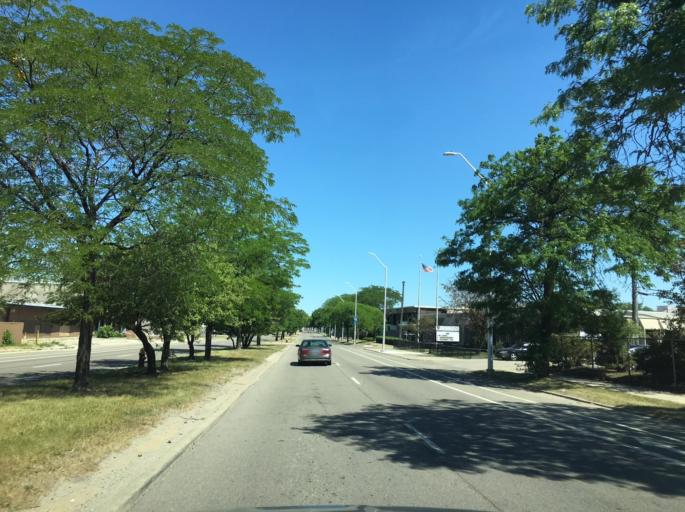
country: US
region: Michigan
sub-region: Wayne County
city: Detroit
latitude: 42.3243
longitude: -83.0678
